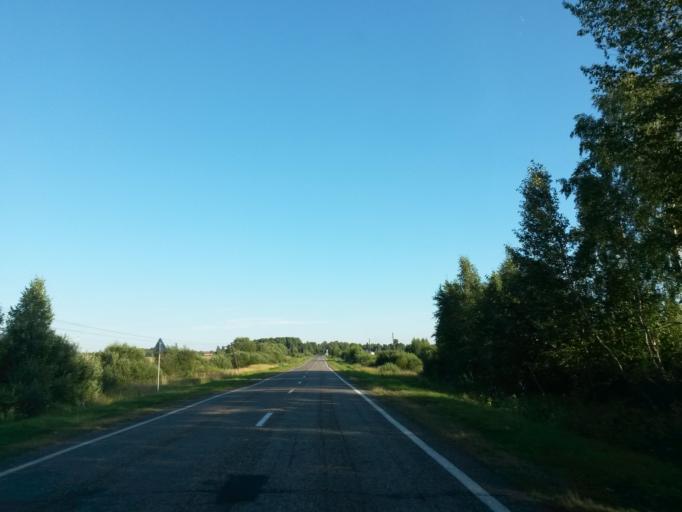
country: RU
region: Jaroslavl
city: Tutayev
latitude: 57.9059
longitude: 39.5213
